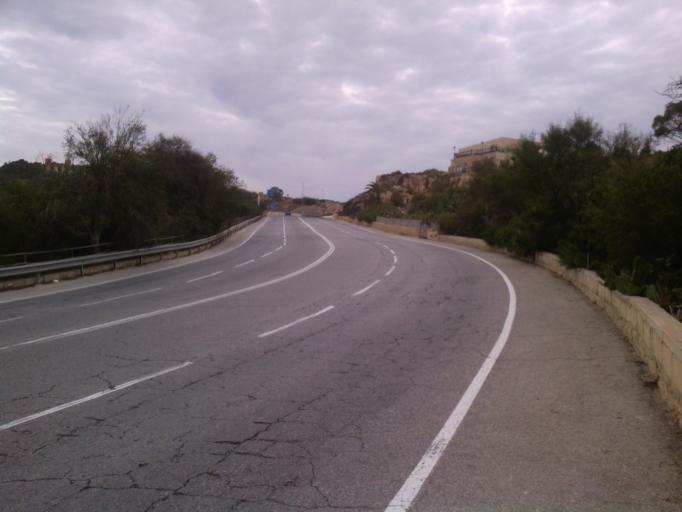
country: MT
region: Il-Mellieha
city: Mellieha
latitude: 35.9755
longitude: 14.3490
